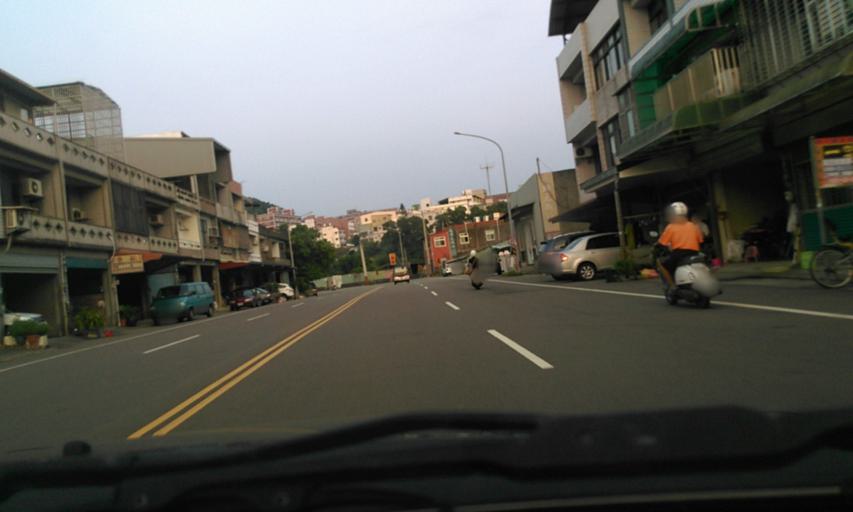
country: TW
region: Taiwan
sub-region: Hsinchu
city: Hsinchu
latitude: 24.6846
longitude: 120.9627
